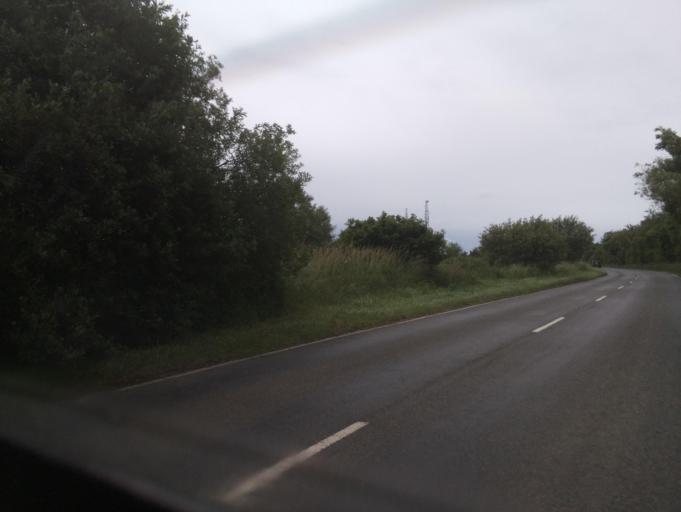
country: GB
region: England
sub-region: Devon
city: Honiton
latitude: 50.7663
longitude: -3.2129
